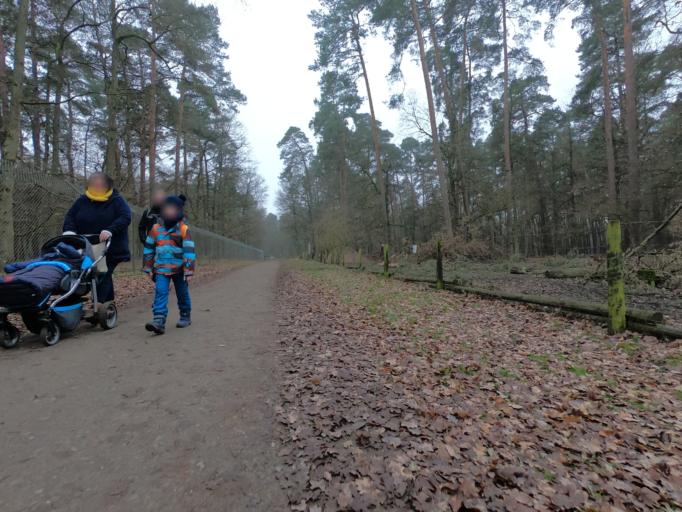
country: DE
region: Hesse
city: Obertshausen
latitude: 50.0813
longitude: 8.9033
